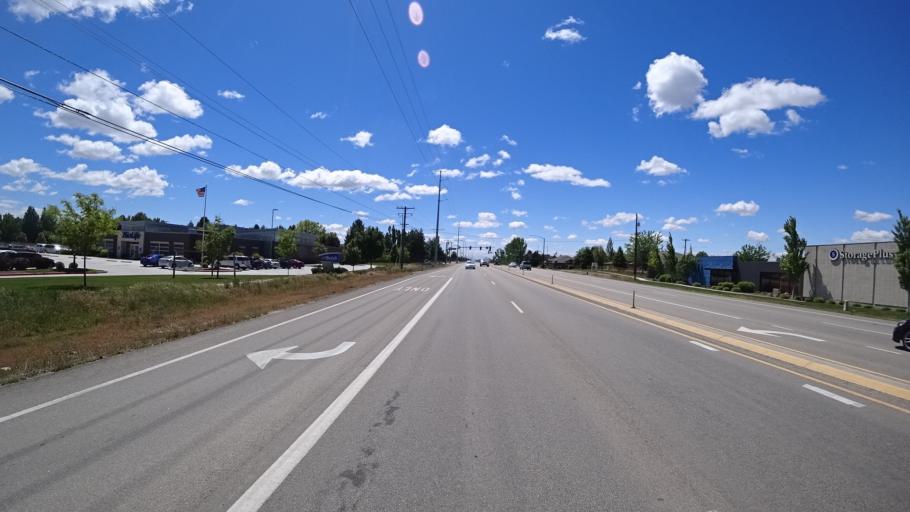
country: US
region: Idaho
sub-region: Ada County
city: Meridian
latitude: 43.6428
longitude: -116.3543
